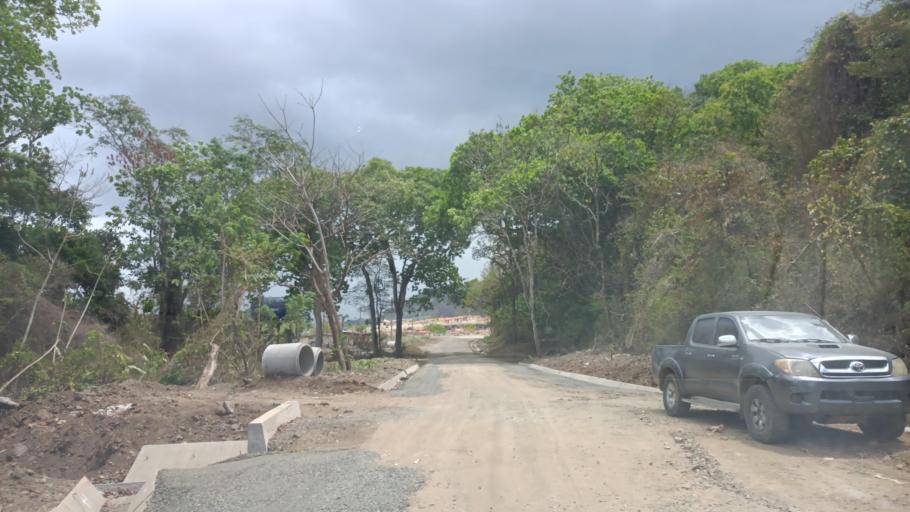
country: PA
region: Panama
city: Las Cumbres
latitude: 9.0656
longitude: -79.5679
